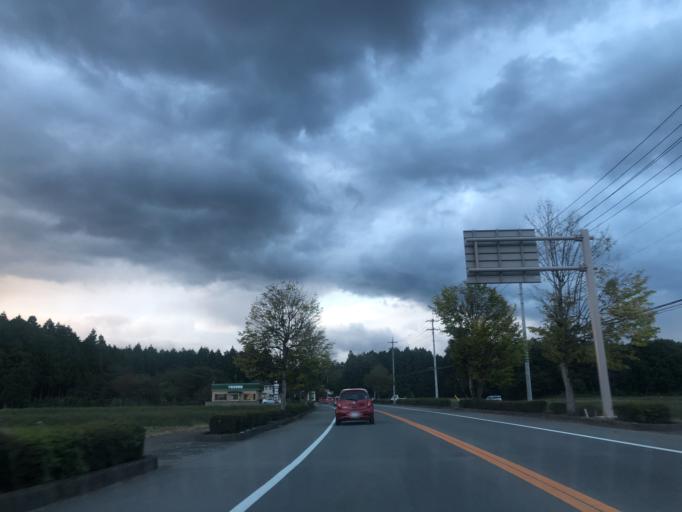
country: JP
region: Tochigi
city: Kuroiso
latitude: 36.9557
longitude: 140.0026
